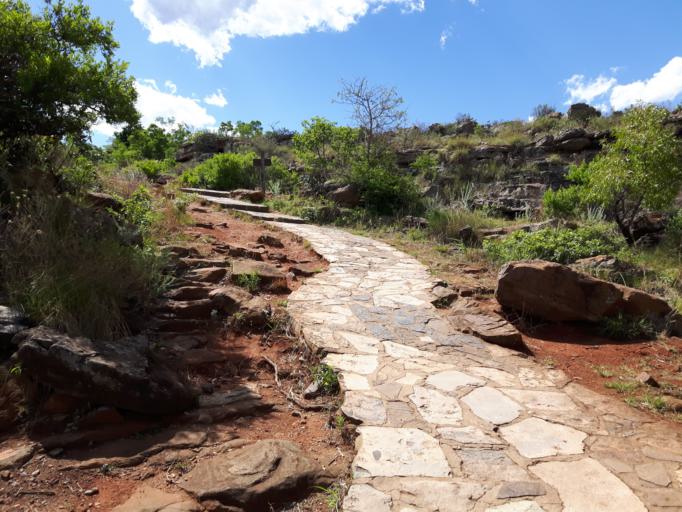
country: ZA
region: Mpumalanga
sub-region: Ehlanzeni District
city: Graksop
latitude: -24.6734
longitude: 30.8098
